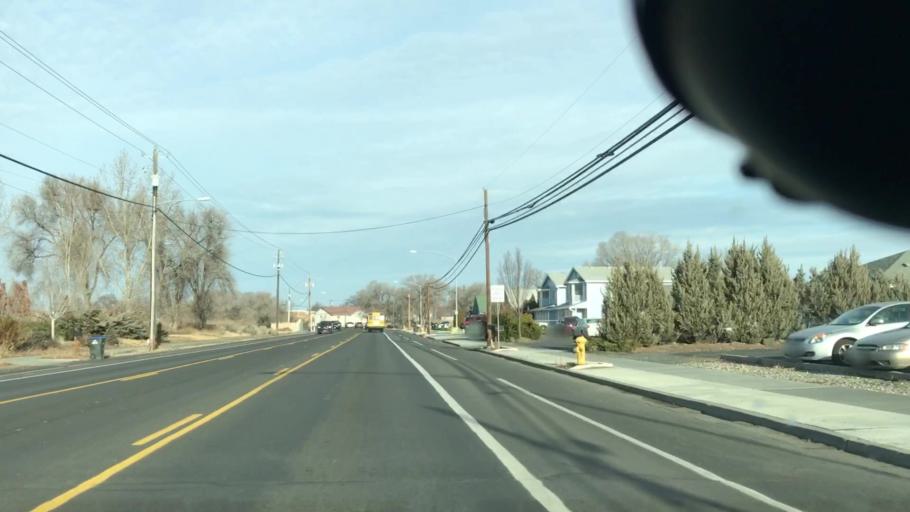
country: US
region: Washington
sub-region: Grant County
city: Moses Lake
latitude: 47.1241
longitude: -119.2740
